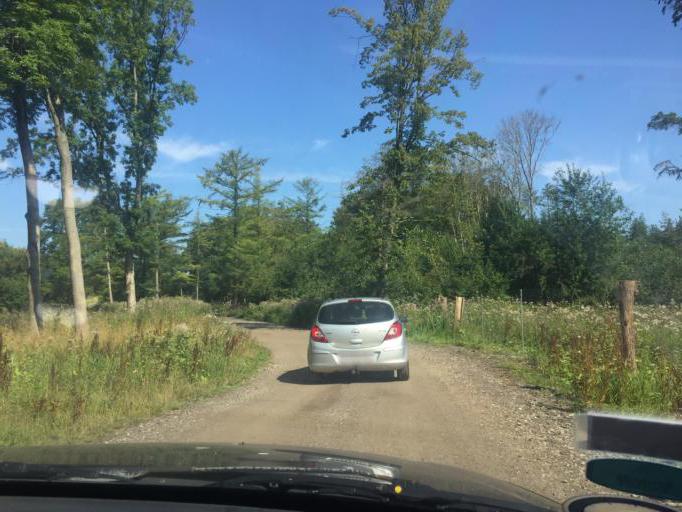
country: DK
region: Zealand
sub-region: Lolland Kommune
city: Maribo
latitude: 54.8146
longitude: 11.5054
